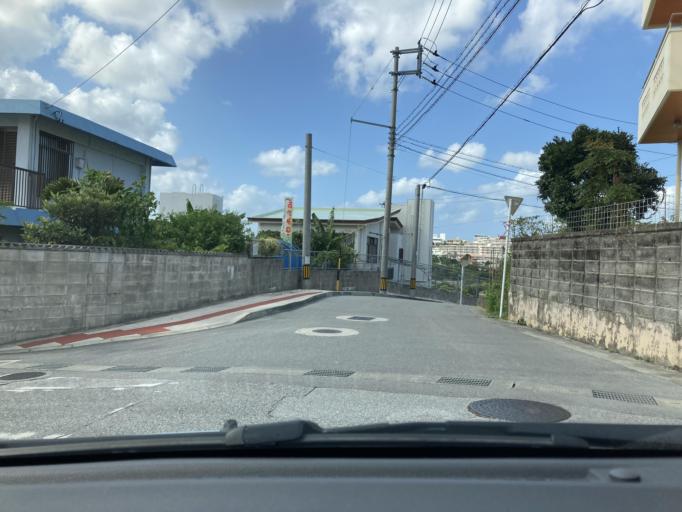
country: JP
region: Okinawa
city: Naha-shi
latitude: 26.2121
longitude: 127.7128
